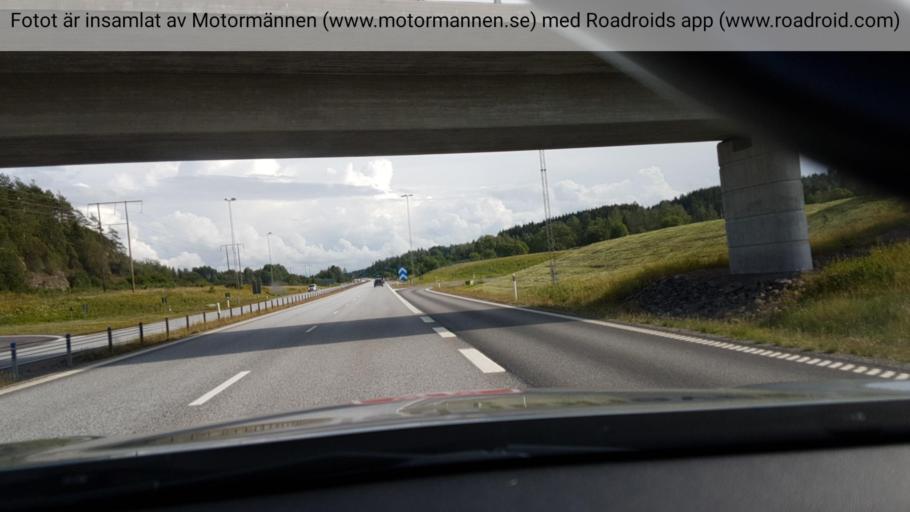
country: SE
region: Vaestra Goetaland
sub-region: Munkedals Kommun
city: Munkedal
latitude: 58.5216
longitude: 11.5479
